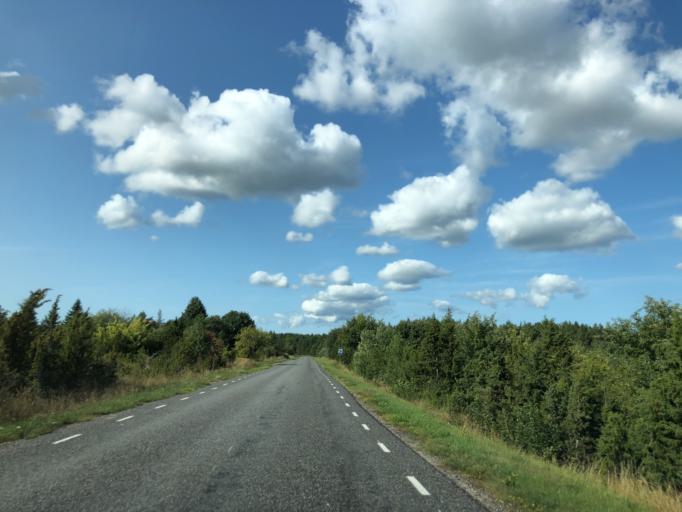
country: EE
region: Hiiumaa
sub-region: Kaerdla linn
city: Kardla
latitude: 58.8026
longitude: 22.7466
